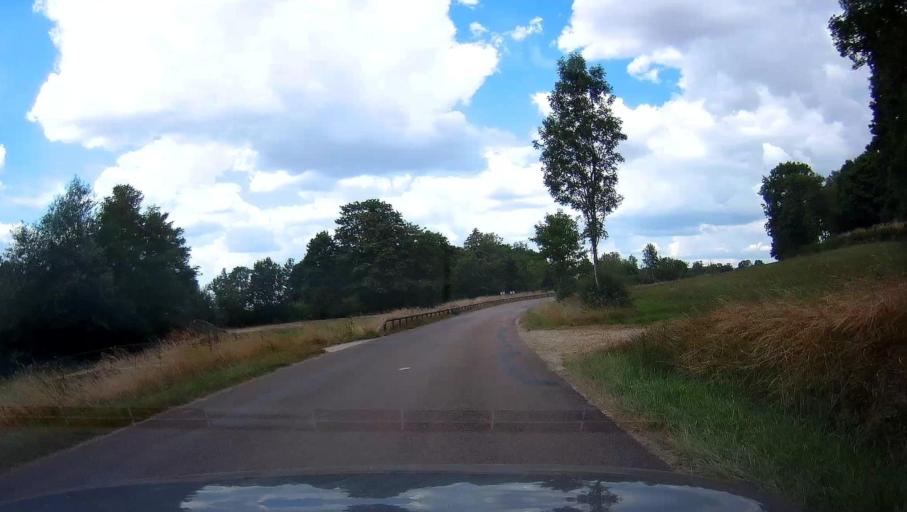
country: FR
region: Champagne-Ardenne
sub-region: Departement de la Haute-Marne
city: Langres
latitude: 47.8604
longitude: 5.3700
